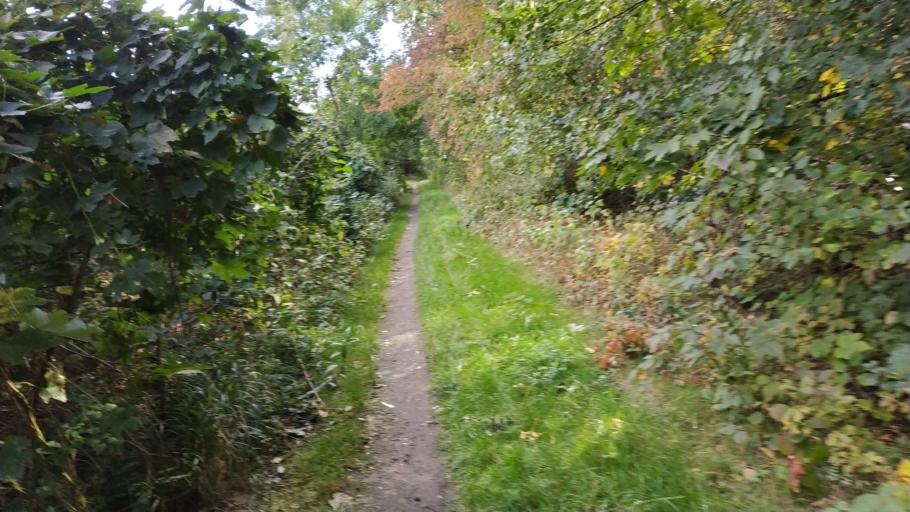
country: PL
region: Lower Silesian Voivodeship
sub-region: Powiat wroclawski
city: Wroclaw
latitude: 51.0712
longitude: 17.0224
